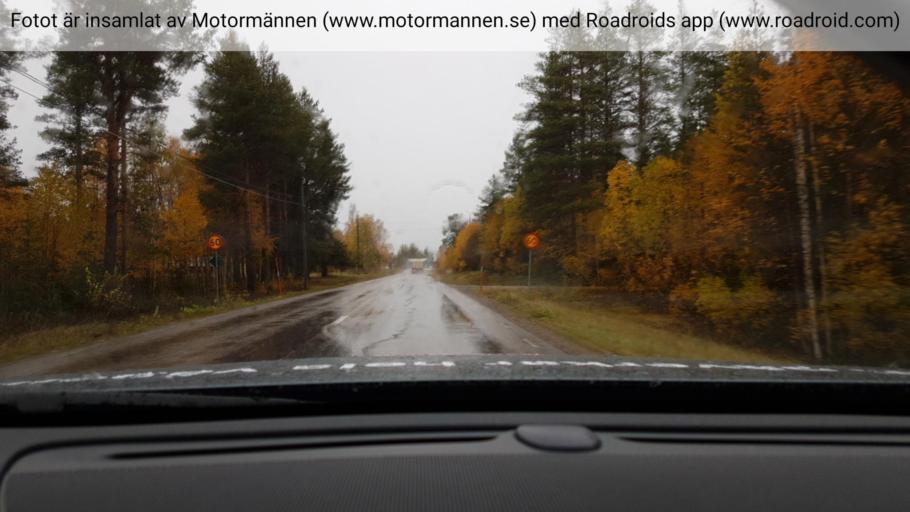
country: SE
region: Norrbotten
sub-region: Overkalix Kommun
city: OEverkalix
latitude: 66.7831
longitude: 22.9119
